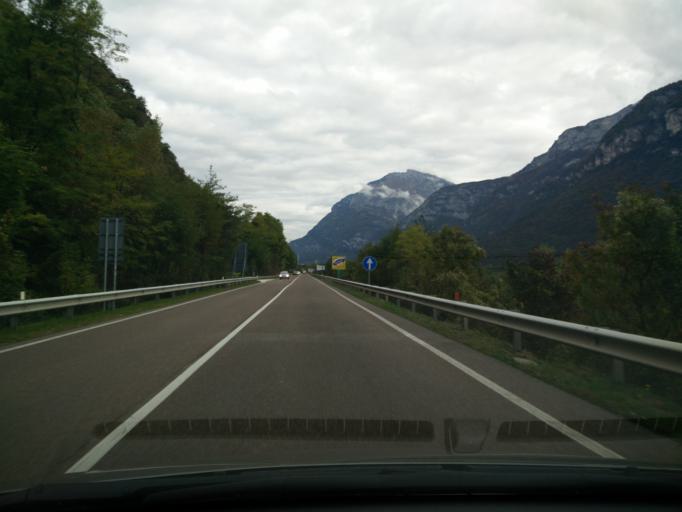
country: IT
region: Veneto
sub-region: Provincia di Belluno
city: Soverzene
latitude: 46.2099
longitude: 12.2863
